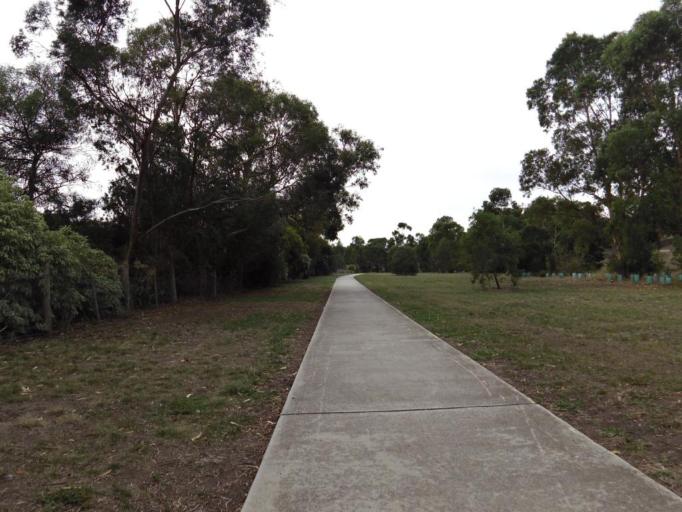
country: AU
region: Victoria
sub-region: Hume
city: Sunbury
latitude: -37.5631
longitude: 144.7233
